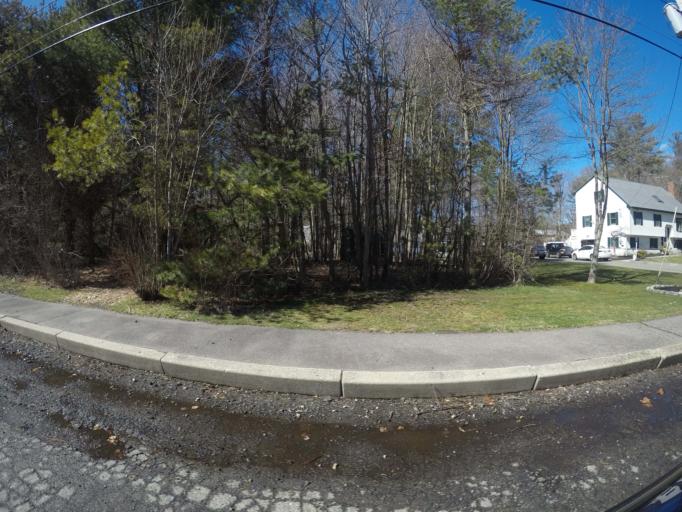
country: US
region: Massachusetts
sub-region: Bristol County
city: Easton
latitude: 42.0063
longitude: -71.1044
